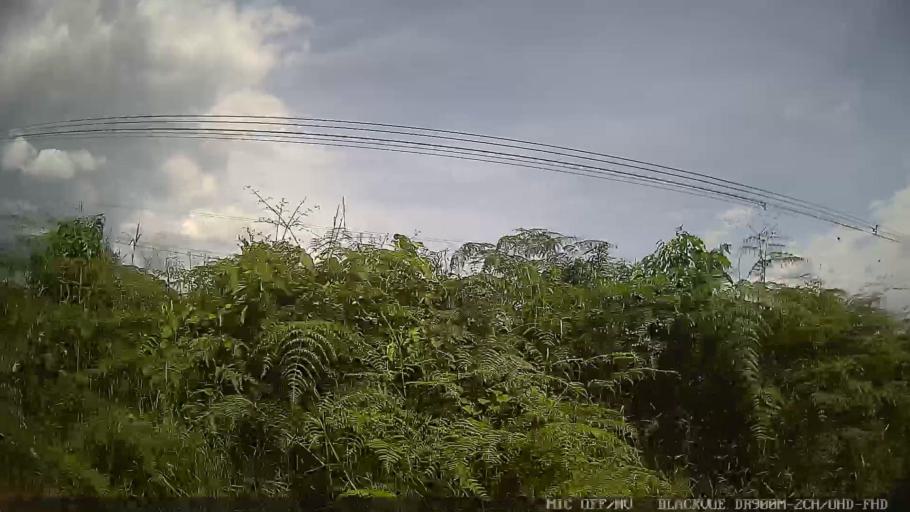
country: BR
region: Sao Paulo
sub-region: Mogi das Cruzes
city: Mogi das Cruzes
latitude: -23.6342
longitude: -46.2106
